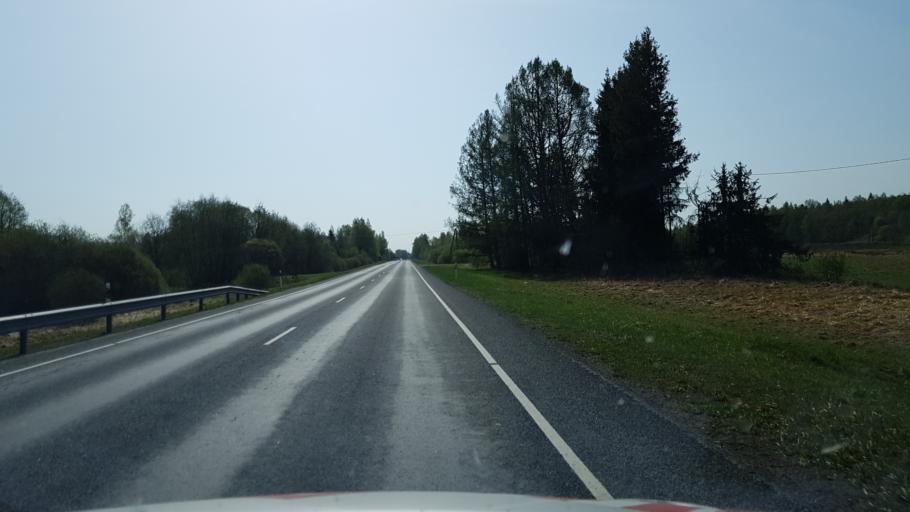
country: EE
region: Paernumaa
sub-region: Saarde vald
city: Kilingi-Nomme
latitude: 58.1850
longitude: 24.7901
